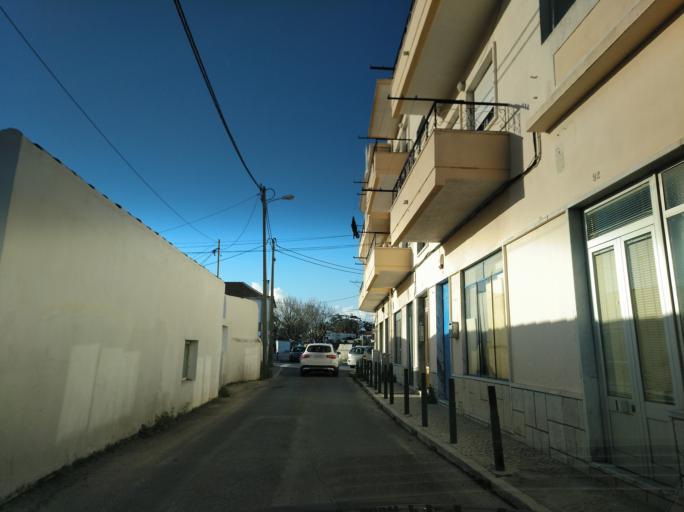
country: PT
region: Setubal
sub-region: Almada
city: Sobreda
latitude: 38.6466
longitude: -9.1917
